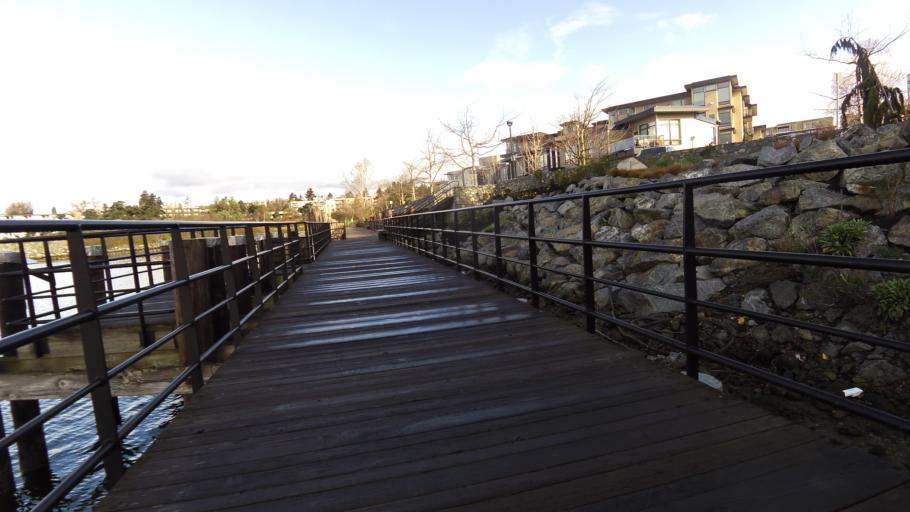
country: CA
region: British Columbia
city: Victoria
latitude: 48.4400
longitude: -123.3796
